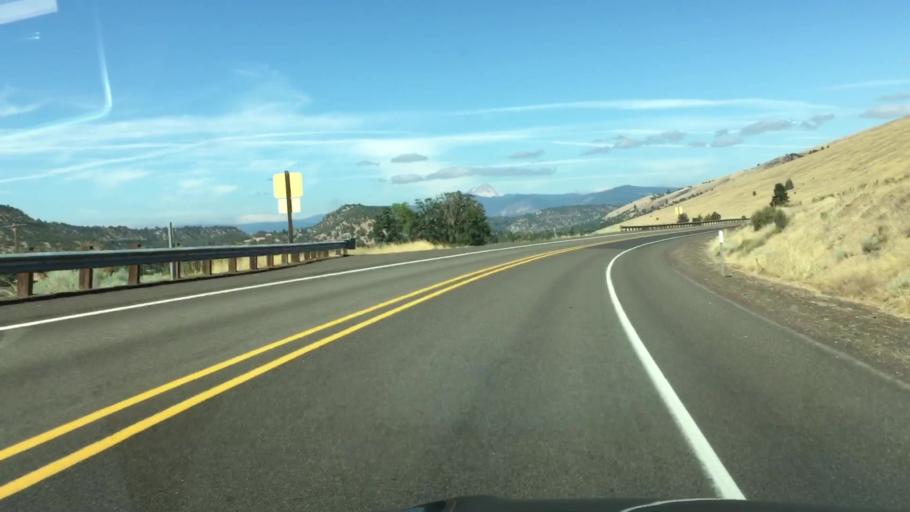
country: US
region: Oregon
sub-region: Wasco County
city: The Dalles
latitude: 45.2548
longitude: -121.1846
